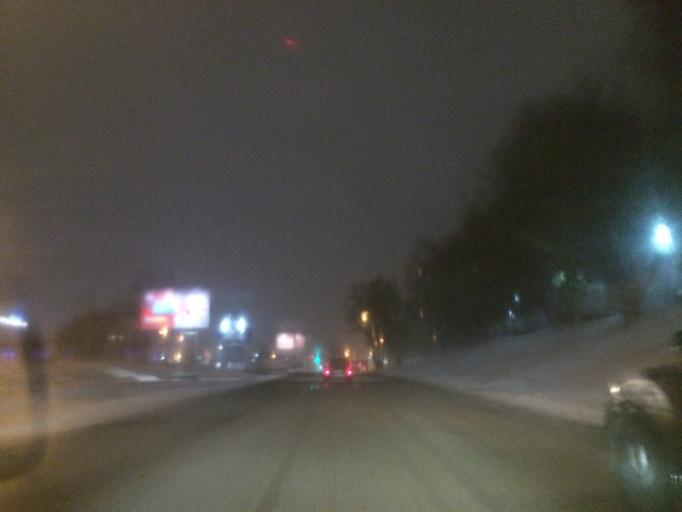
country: RU
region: Tula
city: Mendeleyevskiy
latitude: 54.1569
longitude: 37.5772
